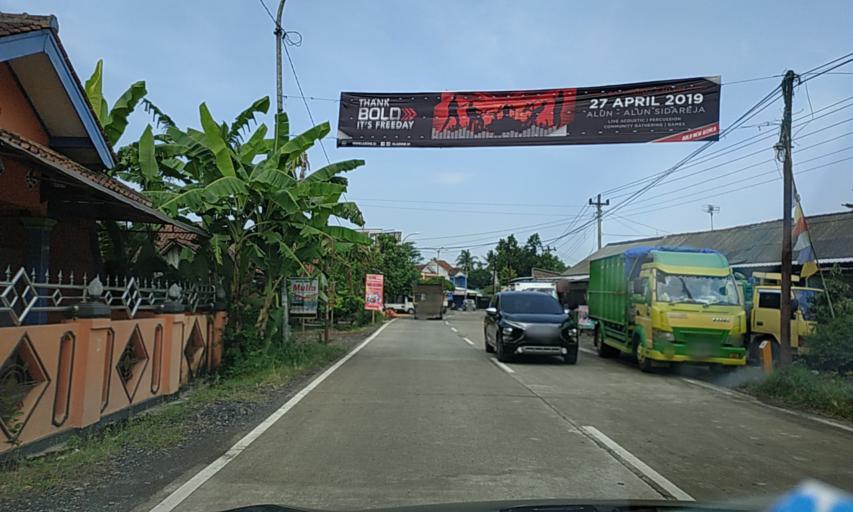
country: ID
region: Central Java
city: Tambangan
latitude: -7.4859
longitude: 108.8210
